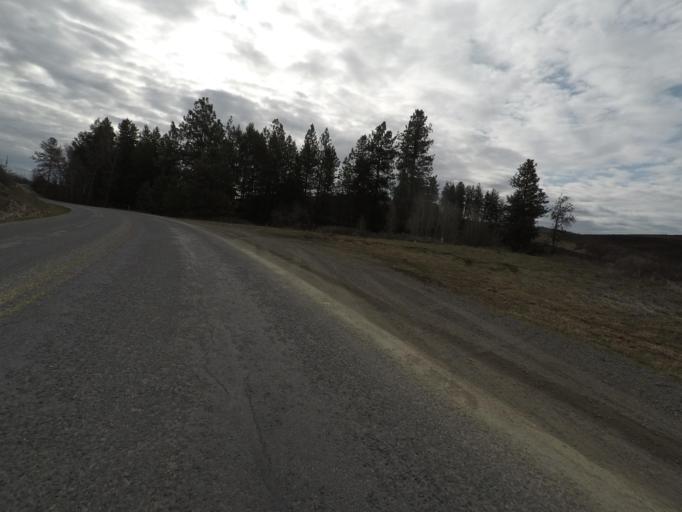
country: US
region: Washington
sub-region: Stevens County
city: Colville
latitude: 48.5188
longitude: -117.8783
